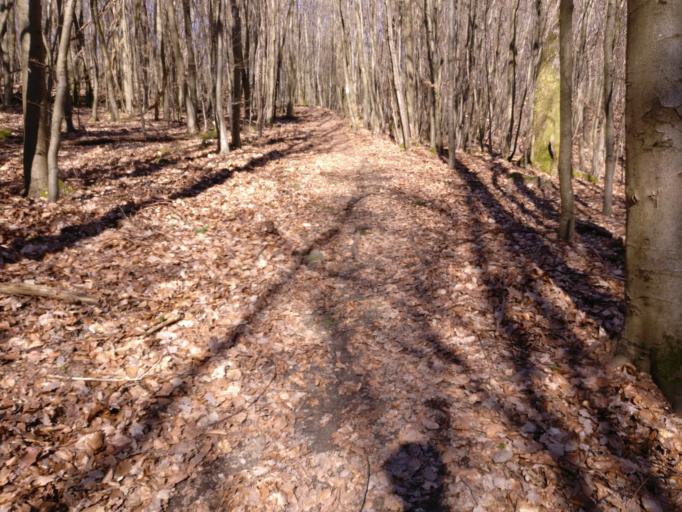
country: DE
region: Hesse
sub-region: Regierungsbezirk Giessen
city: Greifenstein
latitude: 50.6124
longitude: 8.2780
